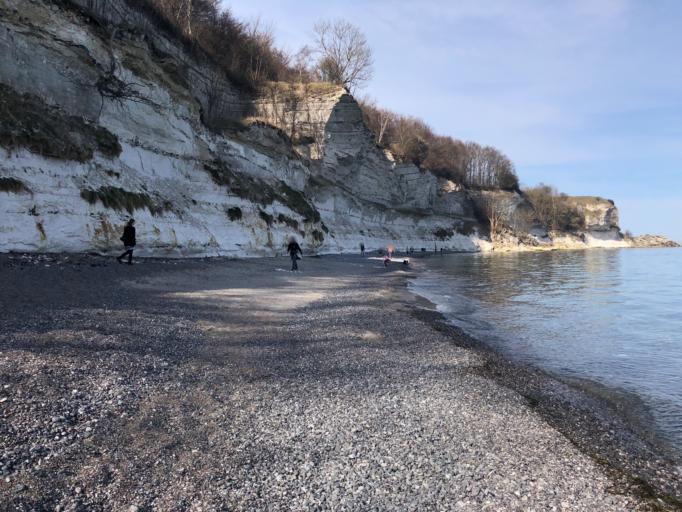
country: DK
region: Zealand
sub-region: Stevns Kommune
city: Store Heddinge
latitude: 55.2800
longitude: 12.4466
